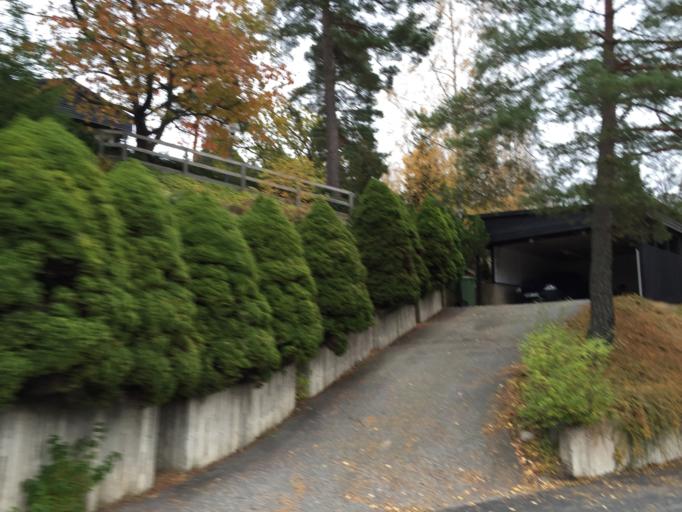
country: SE
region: Stockholm
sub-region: Salems Kommun
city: Ronninge
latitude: 59.2032
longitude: 17.7330
